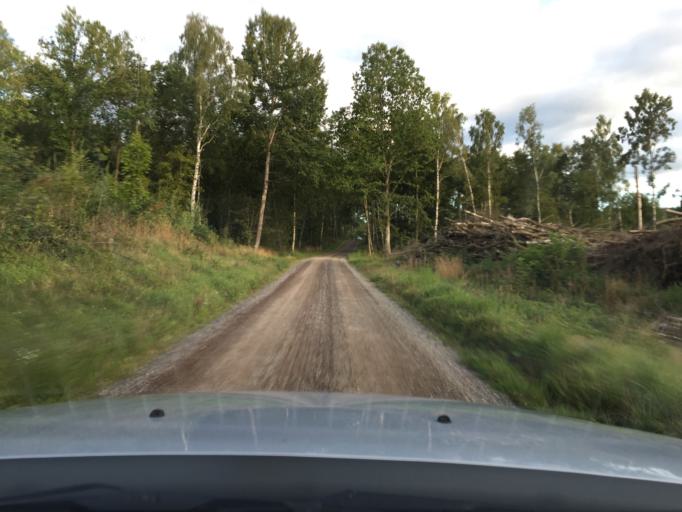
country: SE
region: Skane
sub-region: Hassleholms Kommun
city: Sosdala
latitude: 56.0355
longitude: 13.7130
